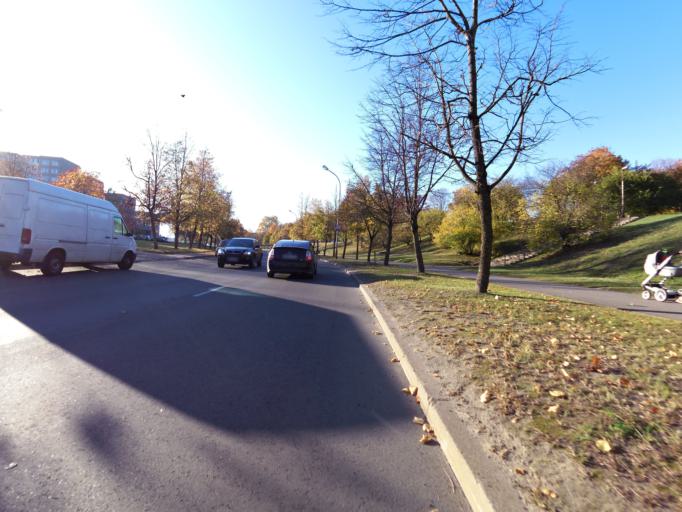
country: LT
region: Vilnius County
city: Pasilaiciai
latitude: 54.7298
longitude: 25.2246
